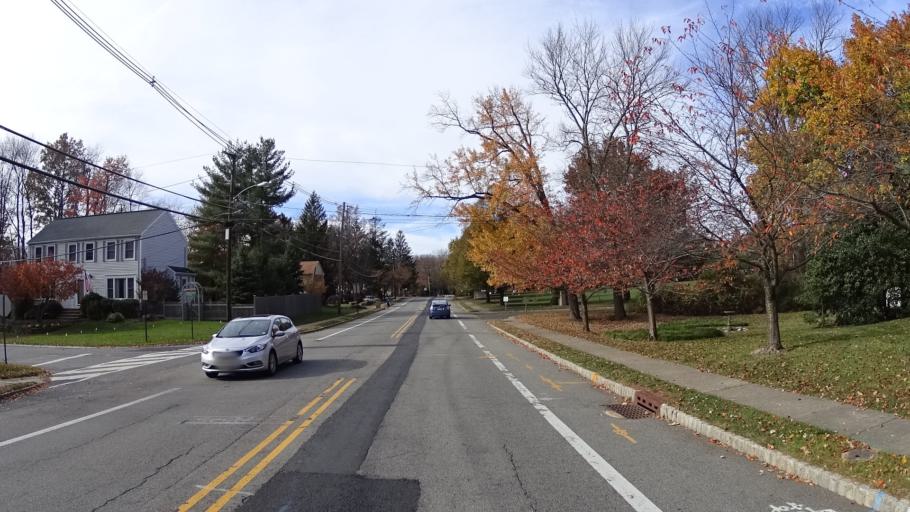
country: US
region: New Jersey
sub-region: Morris County
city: Madison
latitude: 40.7304
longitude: -74.4155
